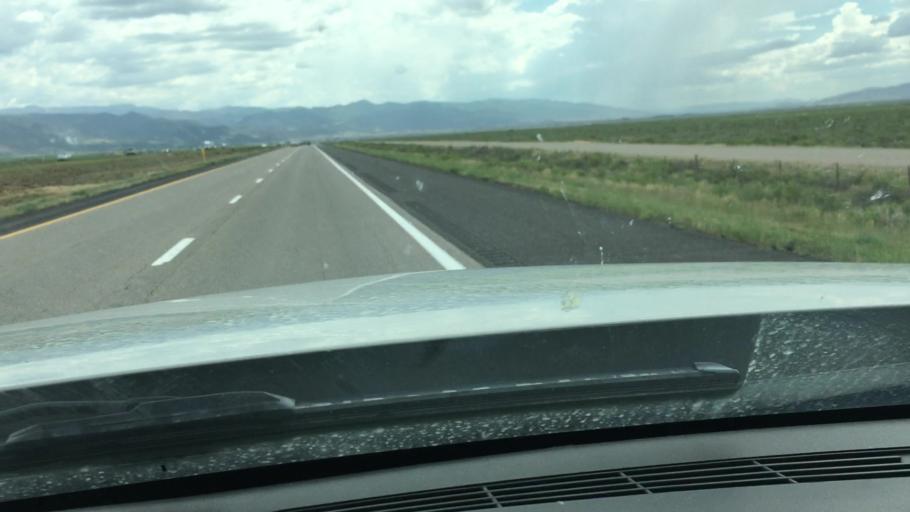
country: US
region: Utah
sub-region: Iron County
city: Parowan
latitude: 37.9659
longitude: -112.7460
